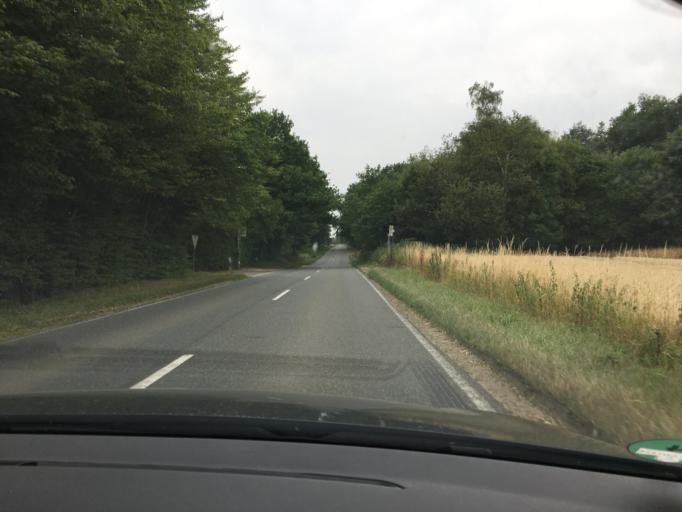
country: DE
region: North Rhine-Westphalia
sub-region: Regierungsbezirk Koln
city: Merzenich
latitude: 50.8612
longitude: 6.5281
